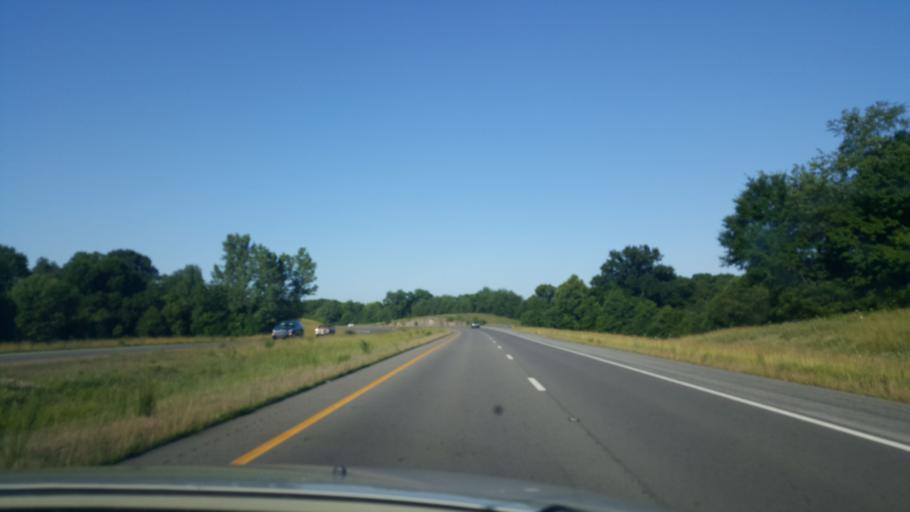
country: US
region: Tennessee
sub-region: Maury County
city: Columbia
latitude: 35.6229
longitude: -87.1156
